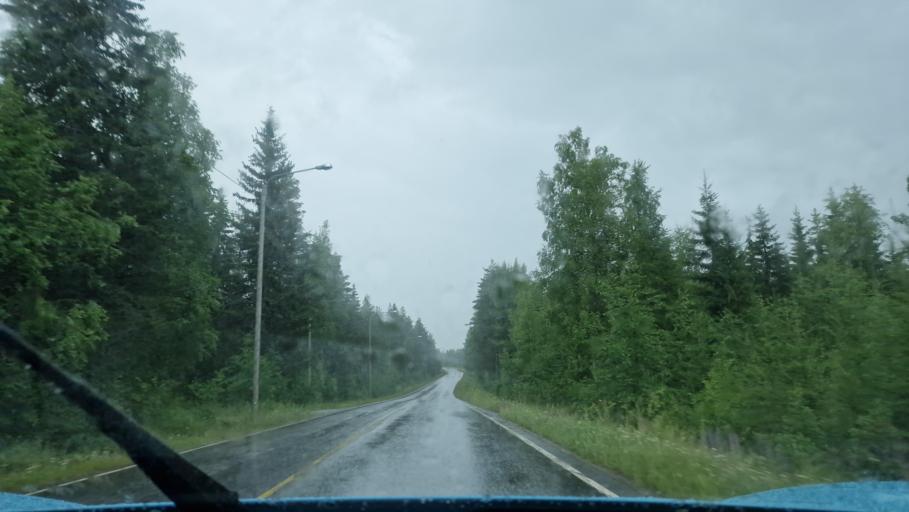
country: FI
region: Southern Ostrobothnia
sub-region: Jaerviseutu
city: Soini
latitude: 62.8376
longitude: 24.3304
